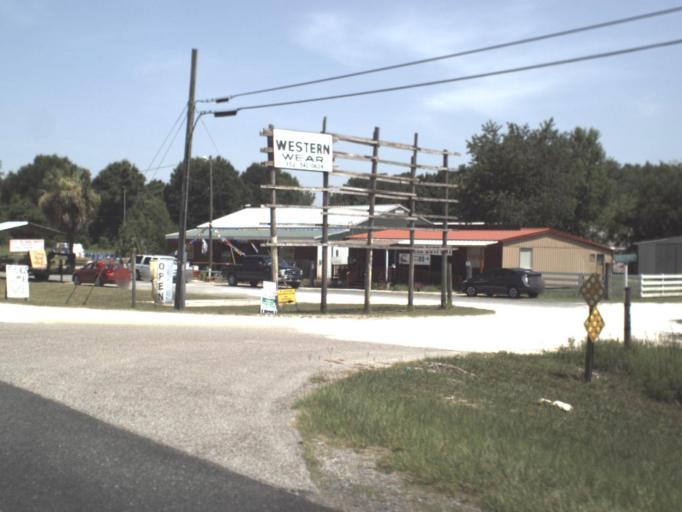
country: US
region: Florida
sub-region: Levy County
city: Manatee Road
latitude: 29.5983
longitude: -82.9734
